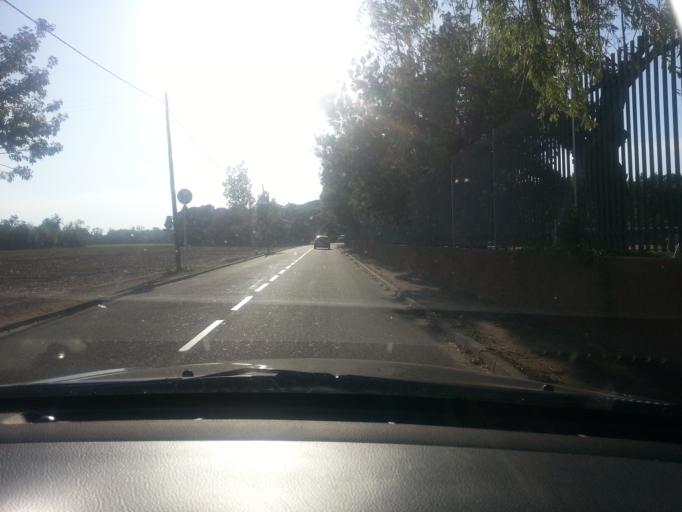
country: ES
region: Catalonia
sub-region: Provincia de Girona
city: Pals
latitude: 42.0100
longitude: 3.1873
